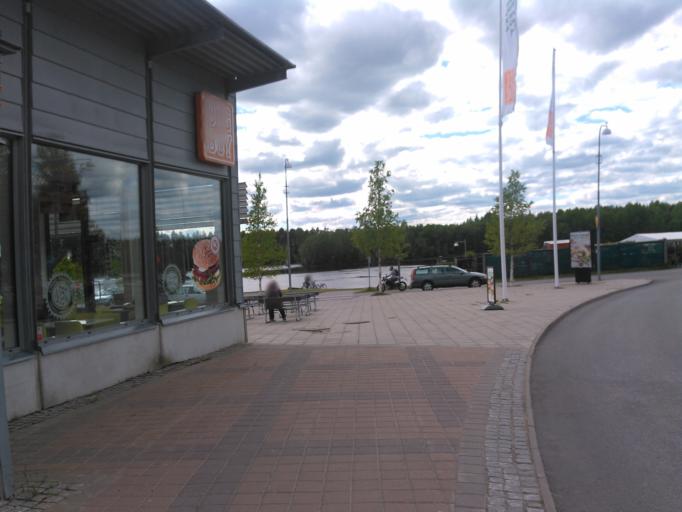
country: SE
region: Vaesterbotten
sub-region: Umea Kommun
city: Umea
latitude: 63.7976
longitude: 20.3024
